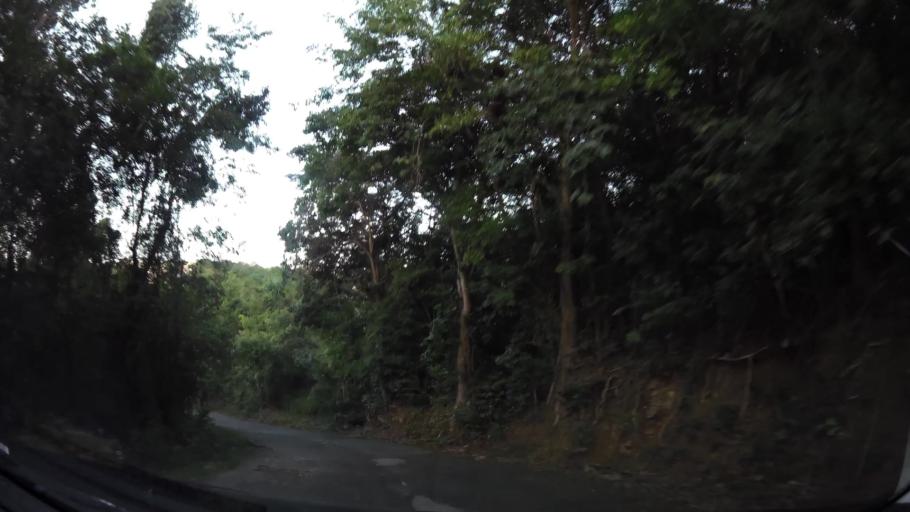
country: VG
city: Tortola
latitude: 18.4484
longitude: -64.5769
